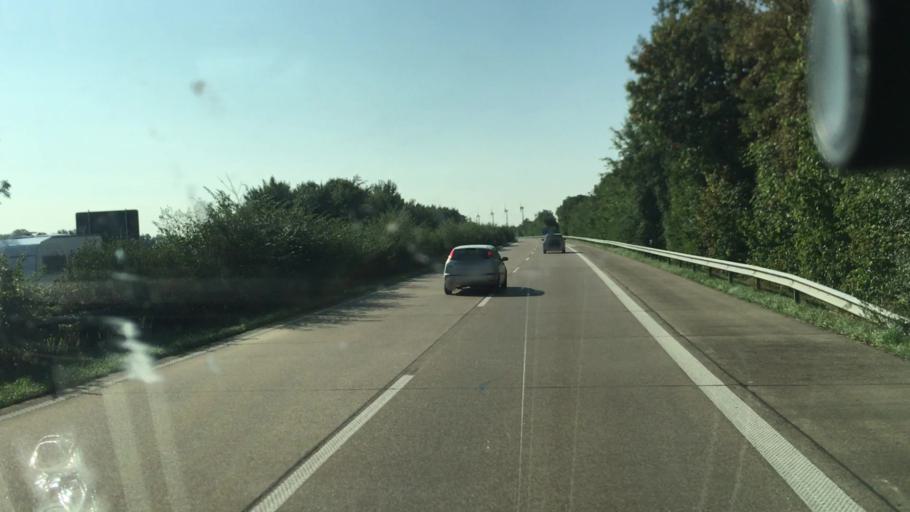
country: DE
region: Lower Saxony
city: Sande
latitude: 53.4627
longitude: 8.0176
